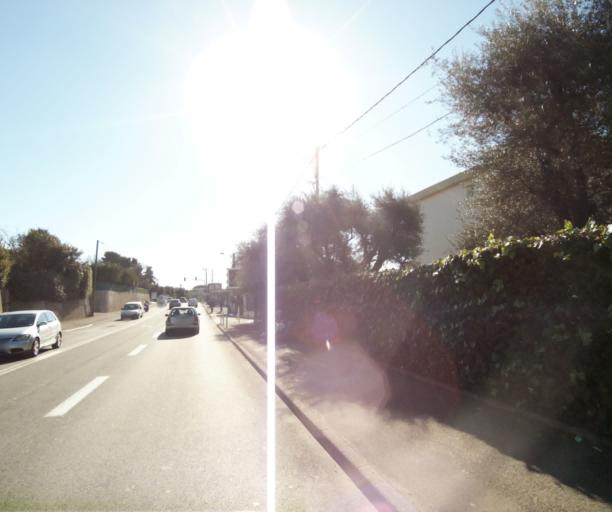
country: FR
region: Provence-Alpes-Cote d'Azur
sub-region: Departement des Alpes-Maritimes
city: Biot
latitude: 43.5971
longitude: 7.1049
